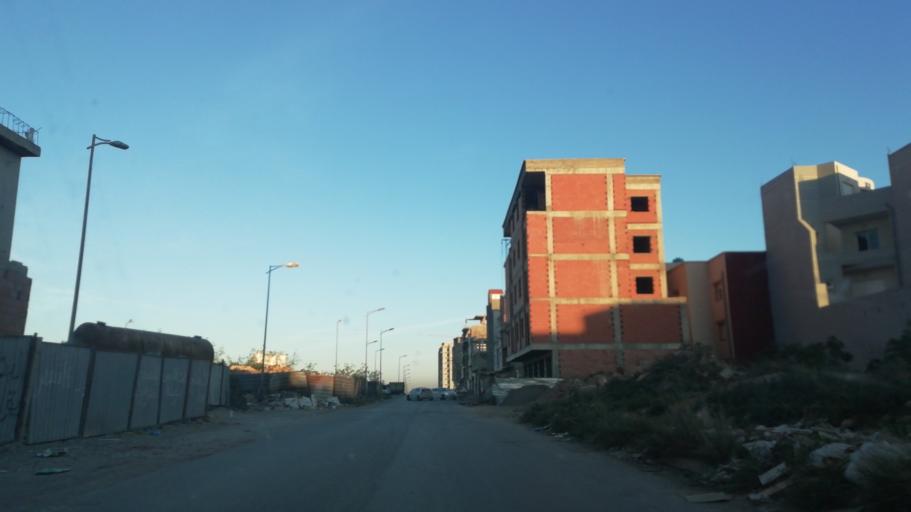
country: DZ
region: Oran
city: Bir el Djir
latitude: 35.7207
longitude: -0.5785
